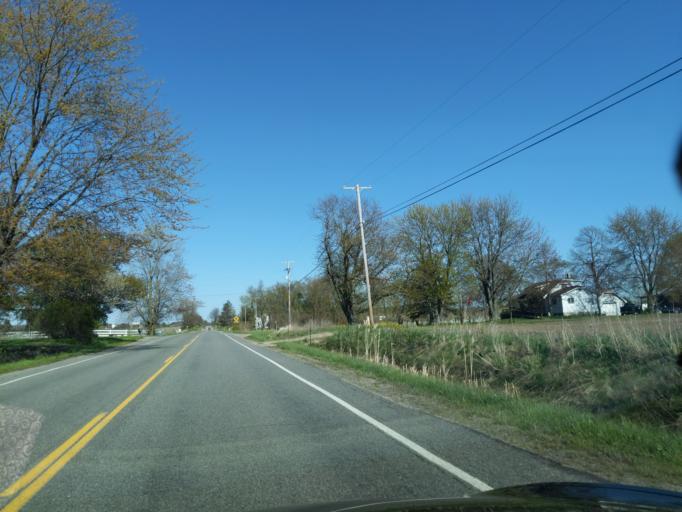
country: US
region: Michigan
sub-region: Kent County
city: Forest Hills
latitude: 42.8853
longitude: -85.4333
